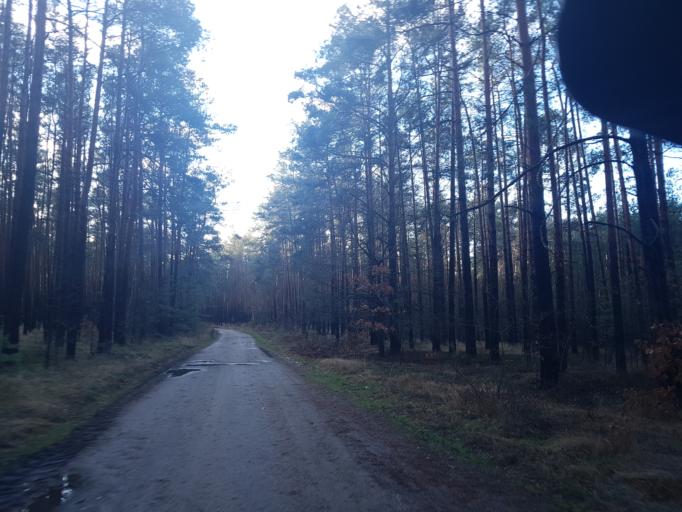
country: DE
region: Brandenburg
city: Ruckersdorf
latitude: 51.5884
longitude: 13.6018
